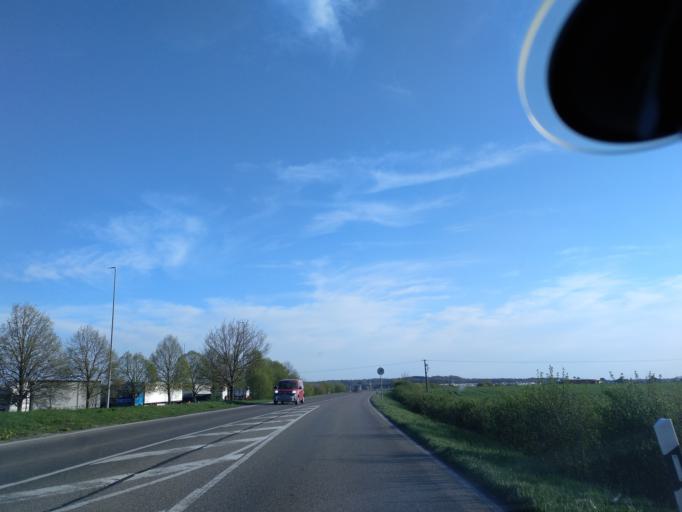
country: DE
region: Baden-Wuerttemberg
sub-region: Regierungsbezirk Stuttgart
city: Kirchberg an der Jagst
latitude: 49.1722
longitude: 9.9599
